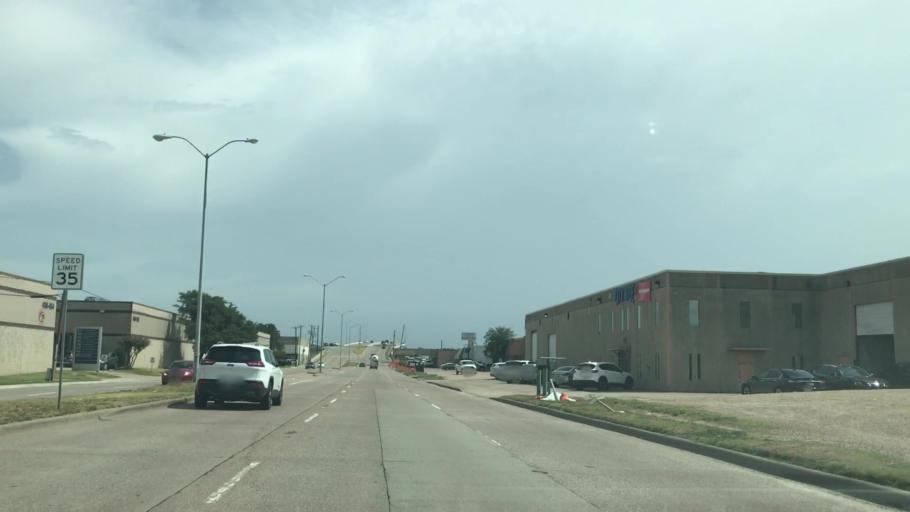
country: US
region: Texas
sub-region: Dallas County
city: Dallas
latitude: 32.8063
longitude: -96.8738
